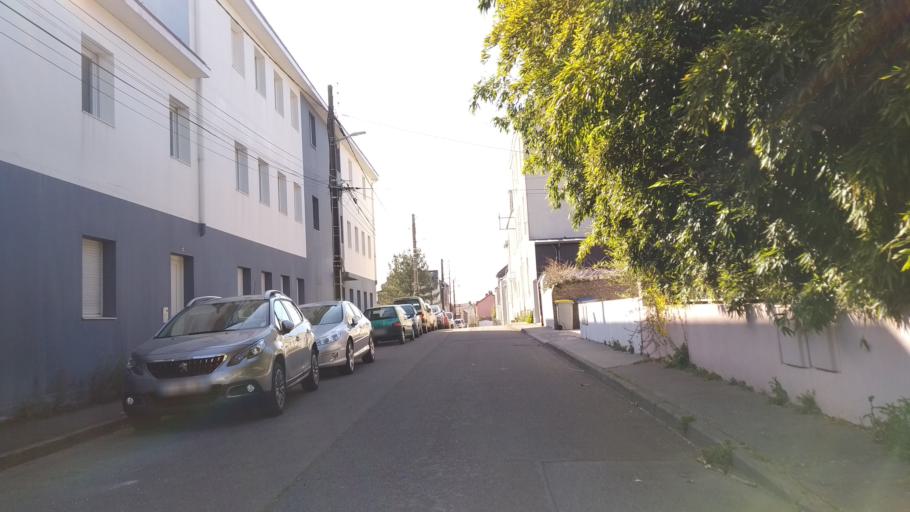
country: FR
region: Pays de la Loire
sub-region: Departement de la Loire-Atlantique
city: Bouguenais
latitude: 47.1992
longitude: -1.5976
